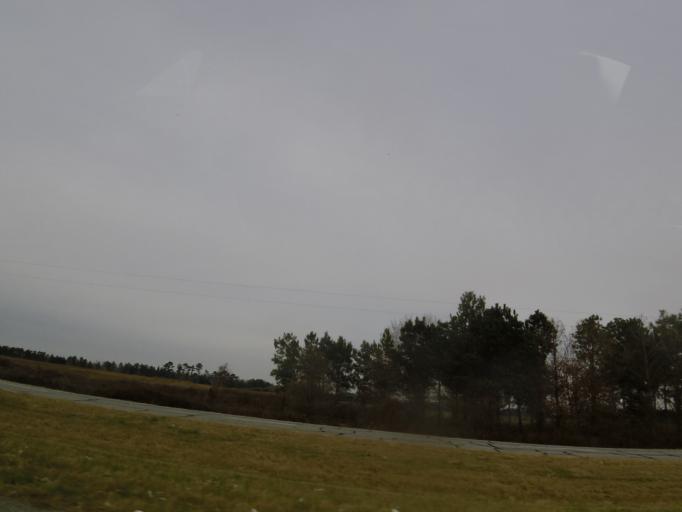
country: US
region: Georgia
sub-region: Decatur County
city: Bainbridge
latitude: 30.9404
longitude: -84.6754
